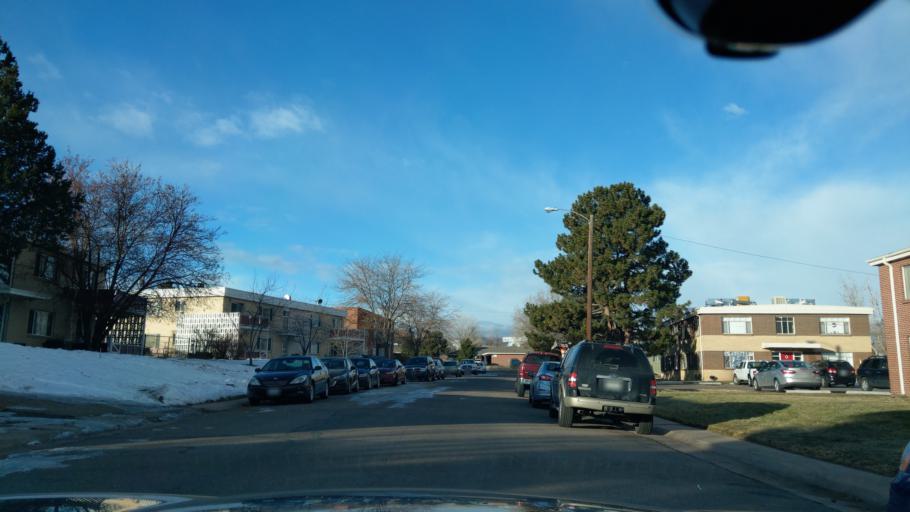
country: US
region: Colorado
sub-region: Jefferson County
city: Lakewood
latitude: 39.7295
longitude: -105.1170
